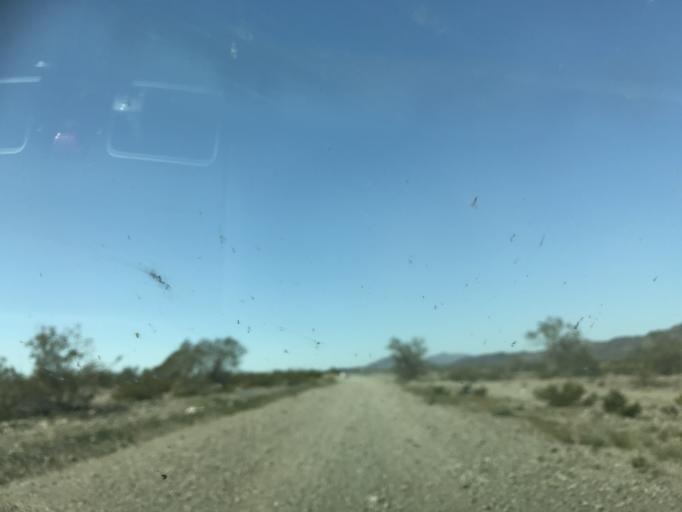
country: US
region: California
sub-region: Riverside County
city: Mesa Verde
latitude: 33.4802
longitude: -114.9311
